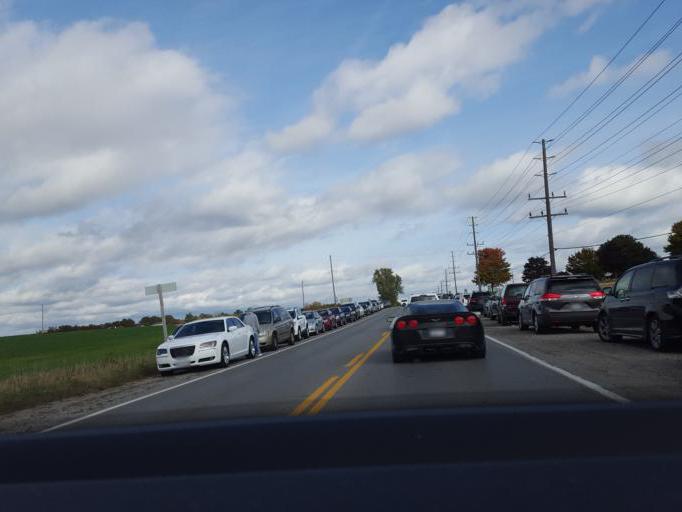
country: CA
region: Ontario
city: Oshawa
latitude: 43.9526
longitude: -78.7931
